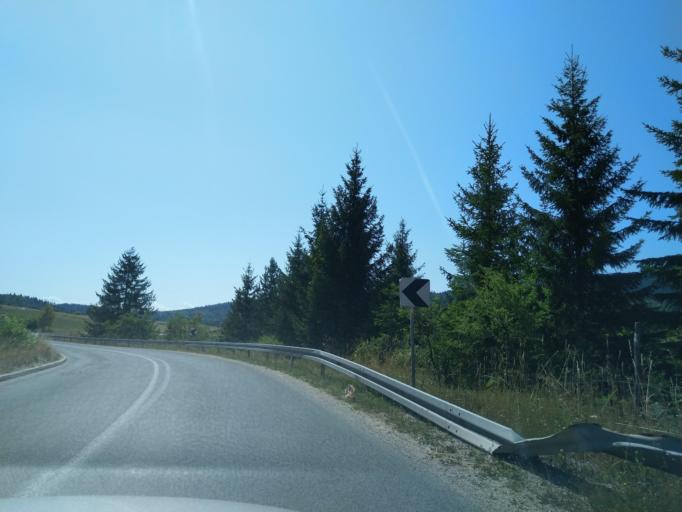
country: RS
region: Central Serbia
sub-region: Zlatiborski Okrug
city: Nova Varos
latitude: 43.4289
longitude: 19.8286
